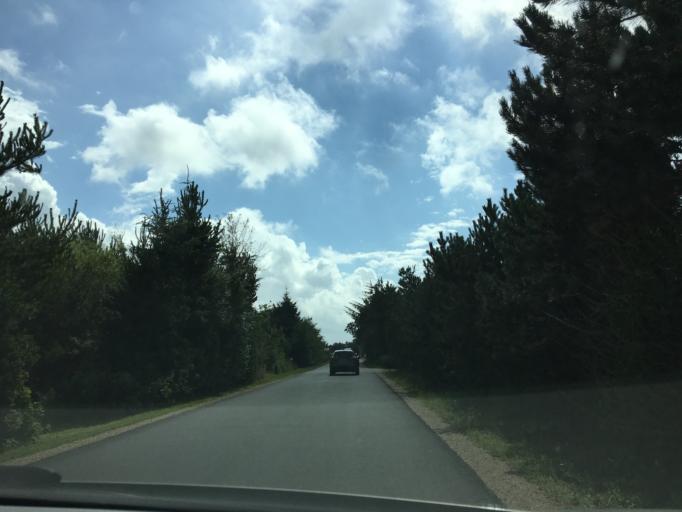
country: DK
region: South Denmark
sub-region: Varde Kommune
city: Oksbol
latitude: 55.7325
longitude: 8.2218
